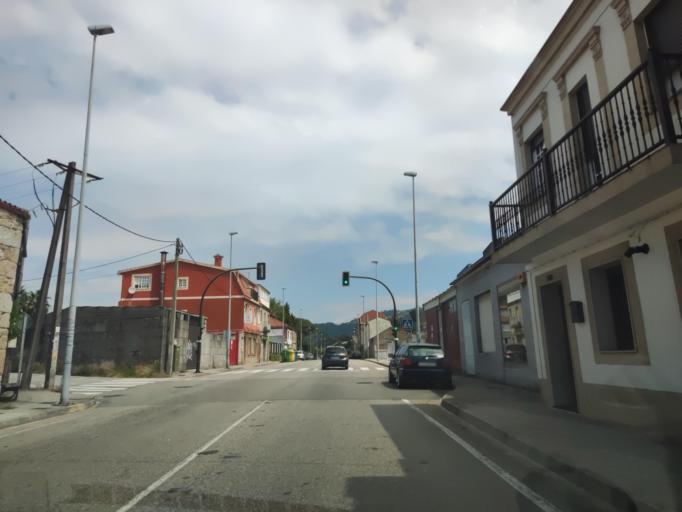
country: ES
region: Galicia
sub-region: Provincia de Pontevedra
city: Vigo
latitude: 42.2555
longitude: -8.6842
